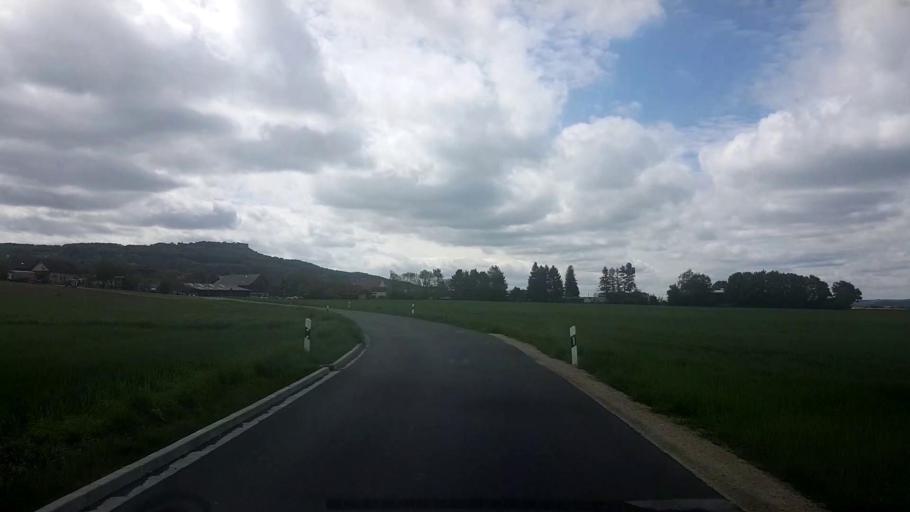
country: DE
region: Bavaria
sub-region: Upper Franconia
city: Bad Staffelstein
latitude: 50.1192
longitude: 11.0315
